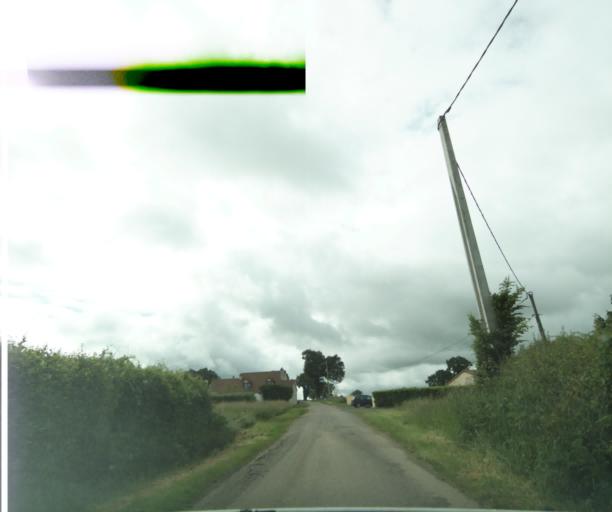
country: FR
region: Bourgogne
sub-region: Departement de Saone-et-Loire
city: Charolles
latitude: 46.4220
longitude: 4.3045
